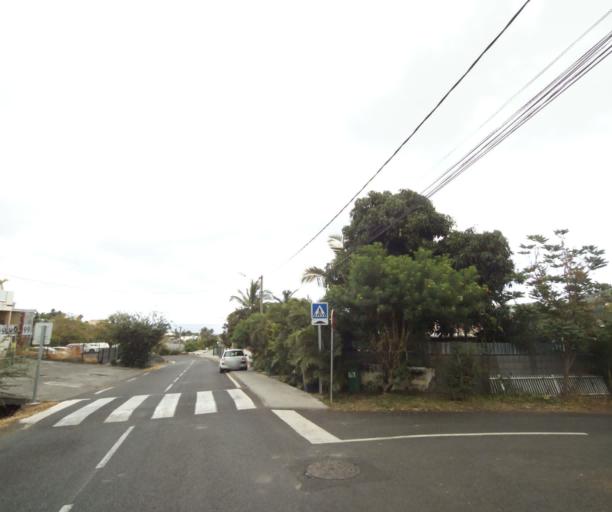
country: RE
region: Reunion
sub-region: Reunion
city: Saint-Paul
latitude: -21.0537
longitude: 55.2319
